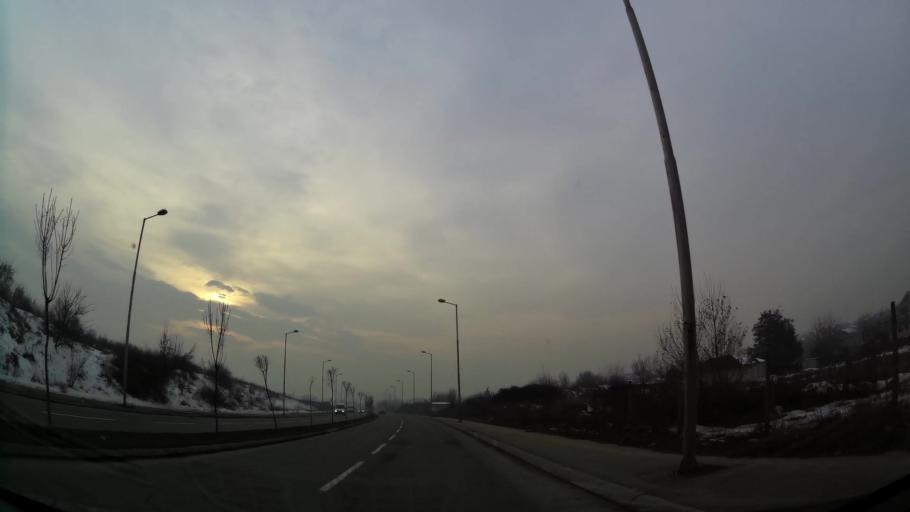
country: MK
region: Suto Orizari
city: Suto Orizare
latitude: 42.0272
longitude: 21.4194
